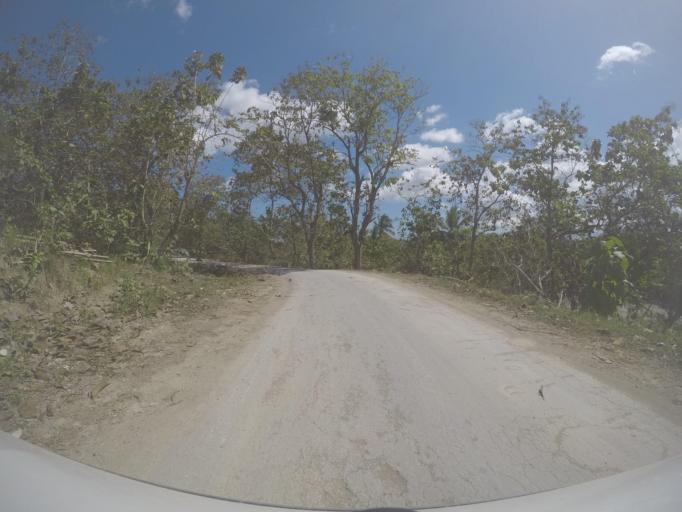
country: TL
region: Viqueque
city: Viqueque
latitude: -8.9038
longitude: 126.3927
